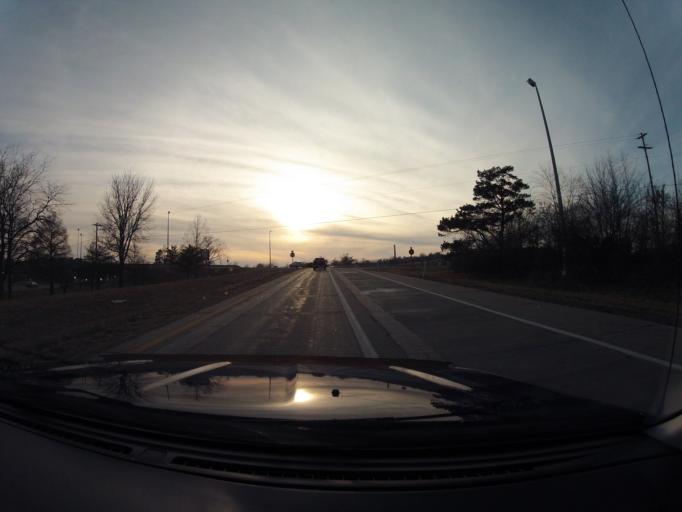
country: US
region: Kansas
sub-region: Shawnee County
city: Topeka
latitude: 39.0614
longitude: -95.7426
